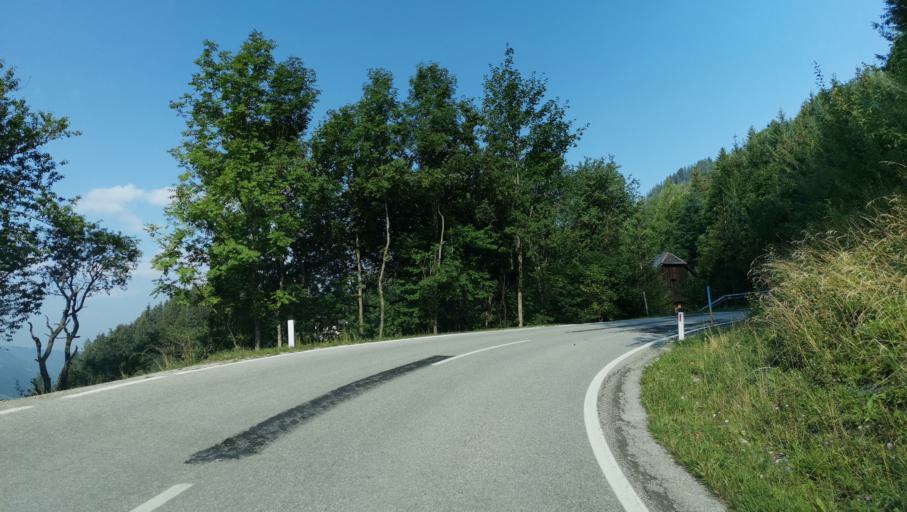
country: AT
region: Styria
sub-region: Politischer Bezirk Liezen
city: Trieben
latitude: 47.5138
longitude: 14.4551
